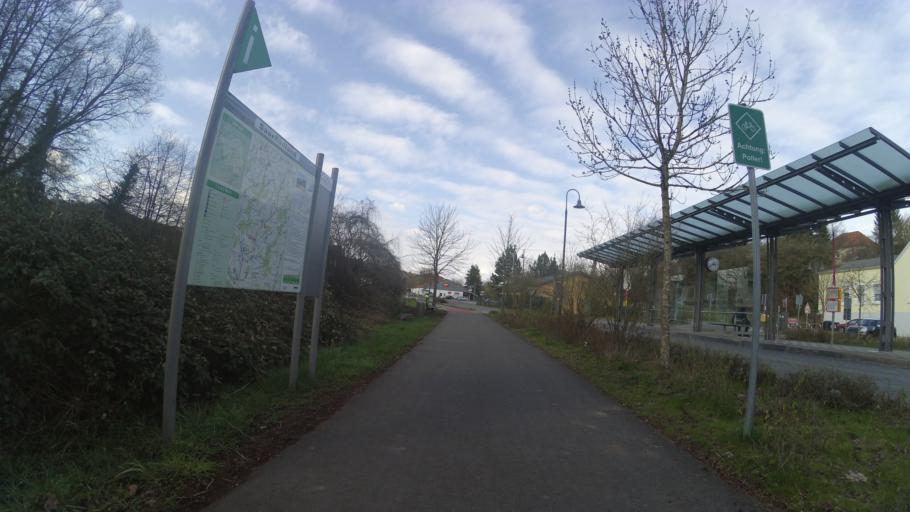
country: DE
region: Saarland
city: Gersheim
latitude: 49.1489
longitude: 7.2095
